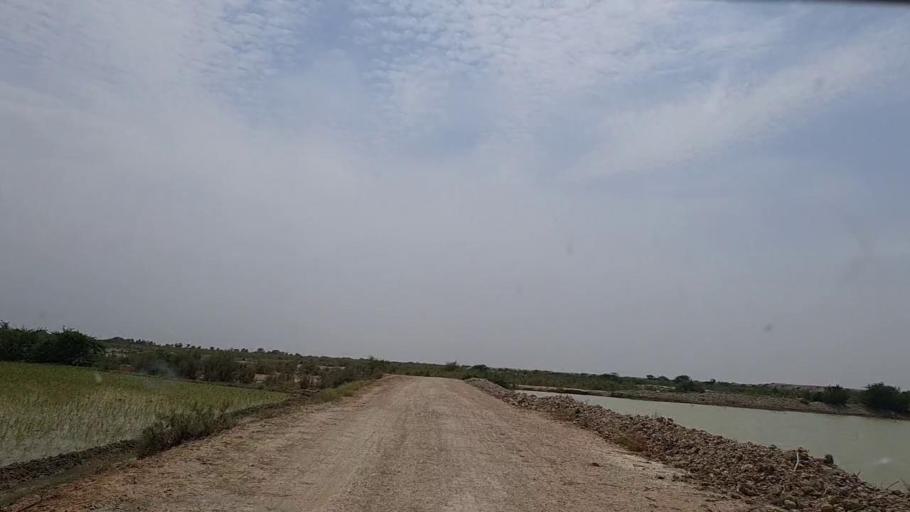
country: PK
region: Sindh
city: Phulji
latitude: 26.8746
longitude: 67.6526
